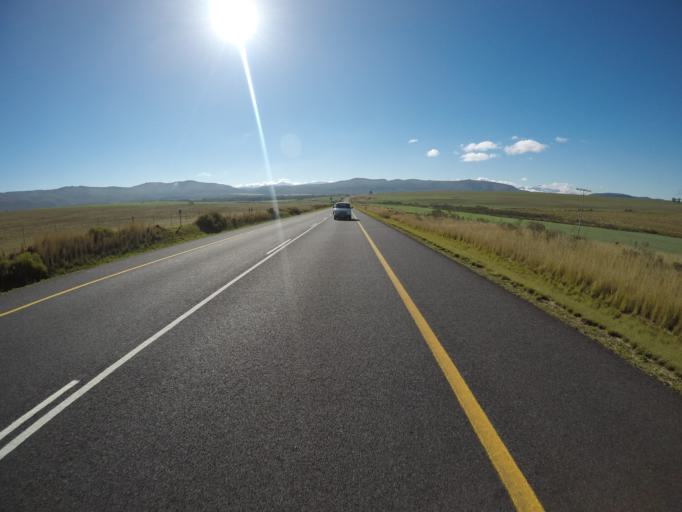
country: ZA
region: Western Cape
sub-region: Cape Winelands District Municipality
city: Ashton
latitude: -34.0992
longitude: 20.0758
